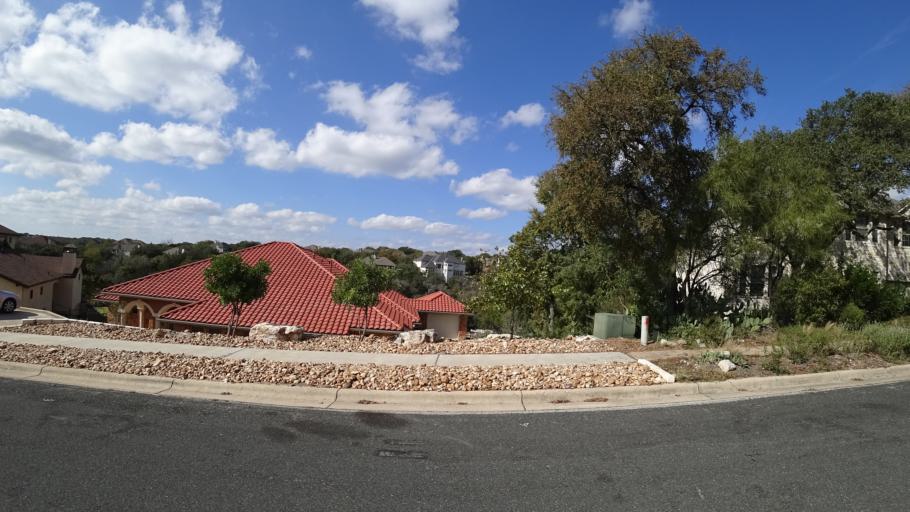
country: US
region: Texas
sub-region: Williamson County
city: Anderson Mill
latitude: 30.4265
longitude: -97.8072
